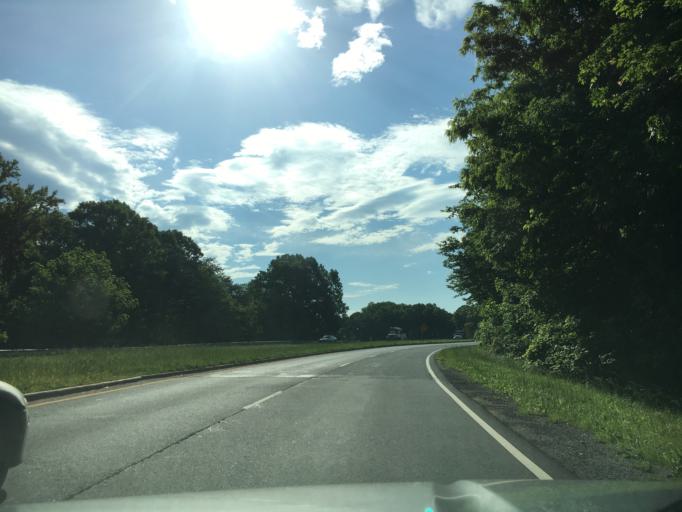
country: US
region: Virginia
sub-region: Campbell County
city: Timberlake
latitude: 37.3323
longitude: -79.2113
